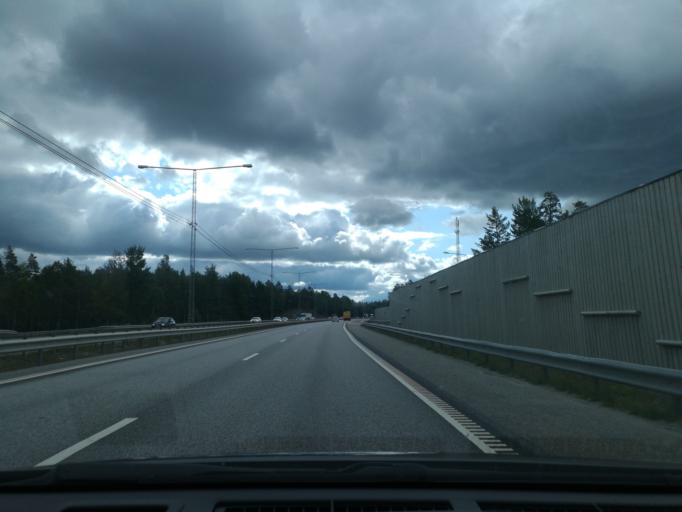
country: SE
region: Stockholm
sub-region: Jarfalla Kommun
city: Jakobsberg
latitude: 59.4495
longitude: 17.8381
